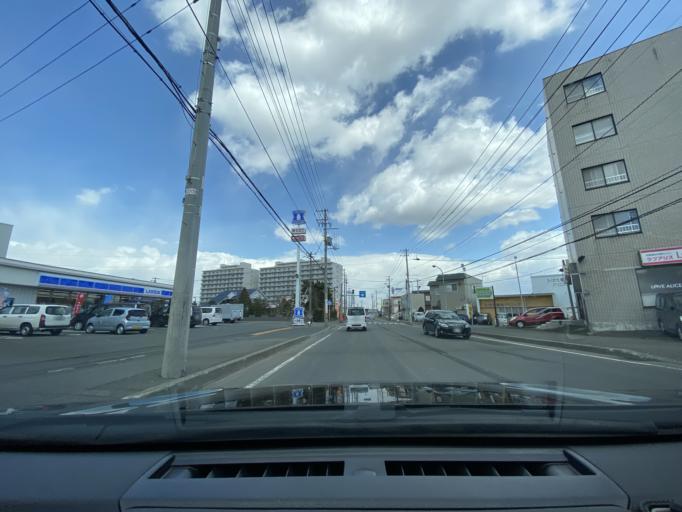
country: JP
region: Hokkaido
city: Kitahiroshima
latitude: 42.9740
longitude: 141.4786
